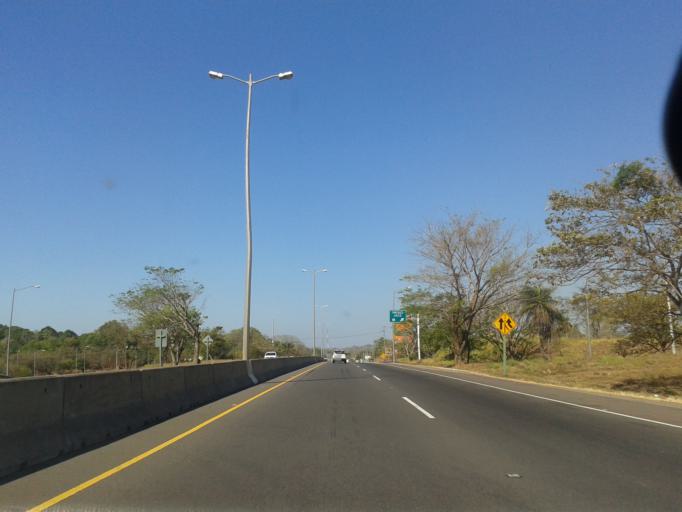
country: CR
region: Alajuela
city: Orotina
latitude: 9.8875
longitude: -84.5741
